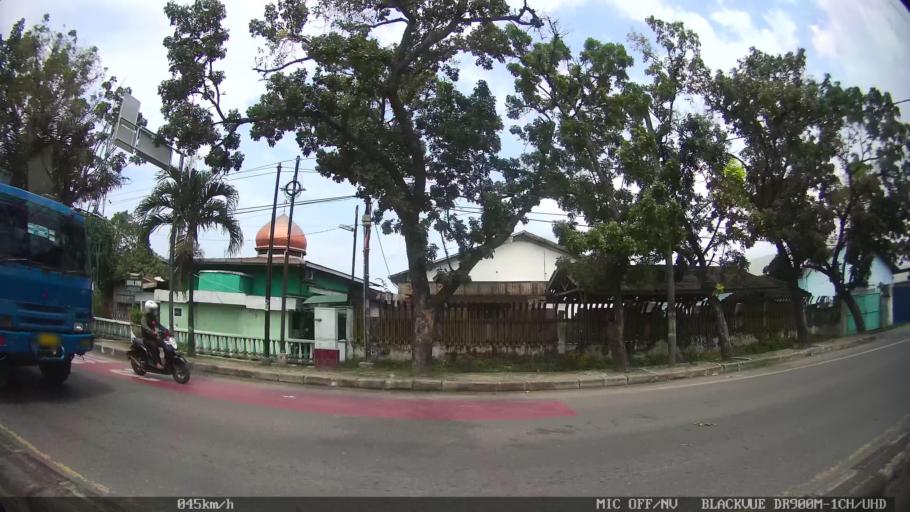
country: ID
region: North Sumatra
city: Medan
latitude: 3.6527
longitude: 98.6636
